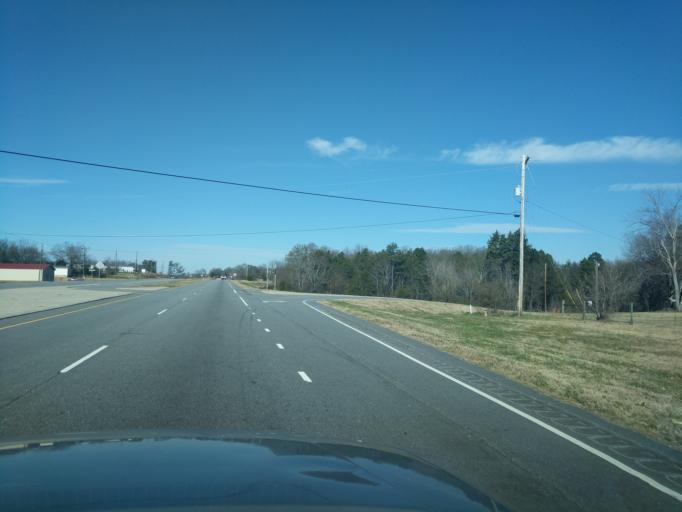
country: US
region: North Carolina
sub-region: Rutherford County
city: Forest City
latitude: 35.2258
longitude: -81.8422
